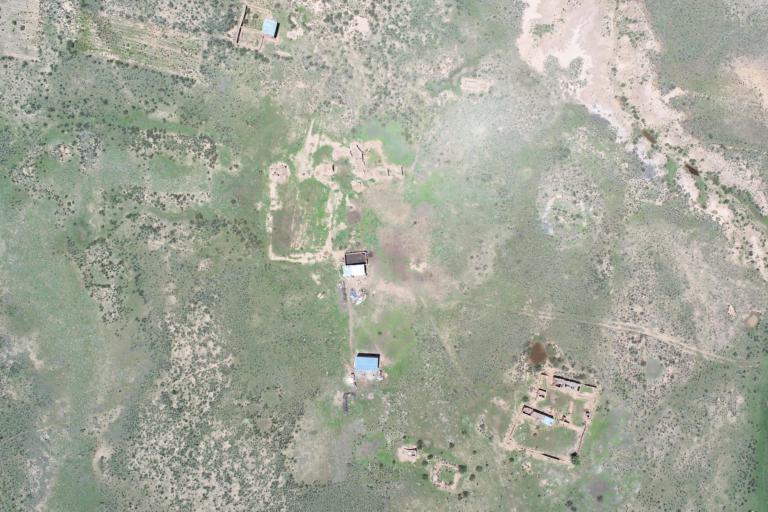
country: BO
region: La Paz
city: Curahuara de Carangas
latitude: -17.3134
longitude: -68.5183
